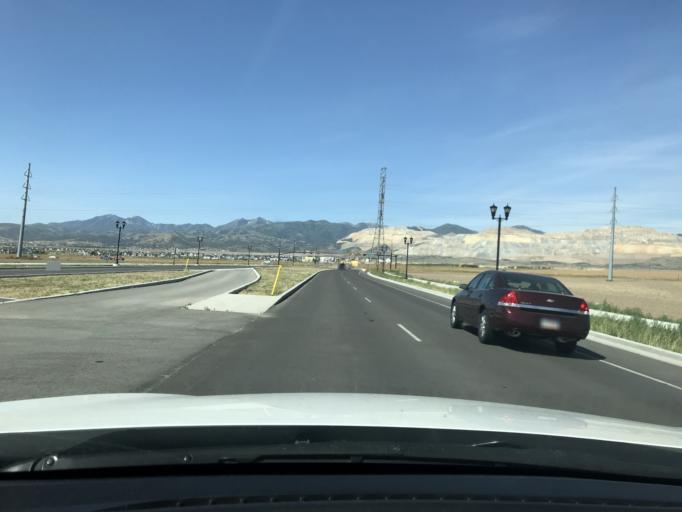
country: US
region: Utah
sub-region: Salt Lake County
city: Herriman
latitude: 40.5531
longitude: -112.0264
